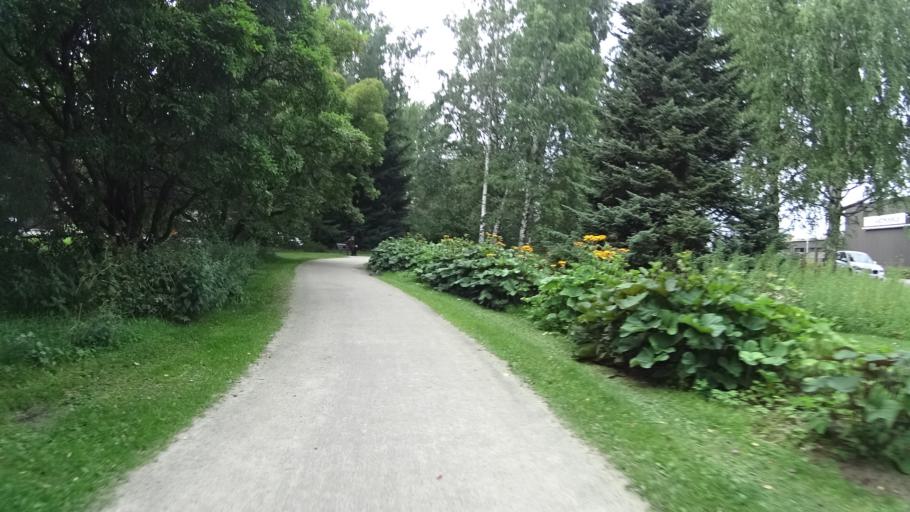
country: FI
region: Uusimaa
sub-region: Helsinki
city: Teekkarikylae
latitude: 60.2359
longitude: 24.8557
